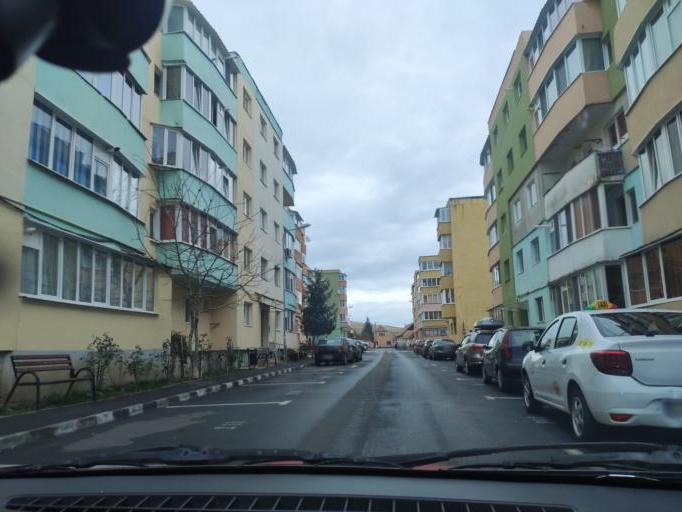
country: RO
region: Brasov
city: Codlea
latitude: 45.7029
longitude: 25.4425
